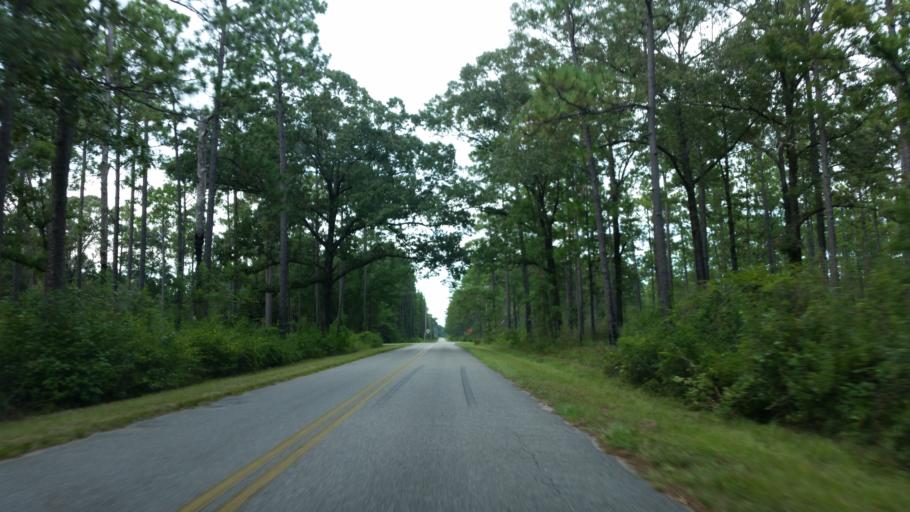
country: US
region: Florida
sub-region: Santa Rosa County
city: Point Baker
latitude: 30.7323
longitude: -86.8749
